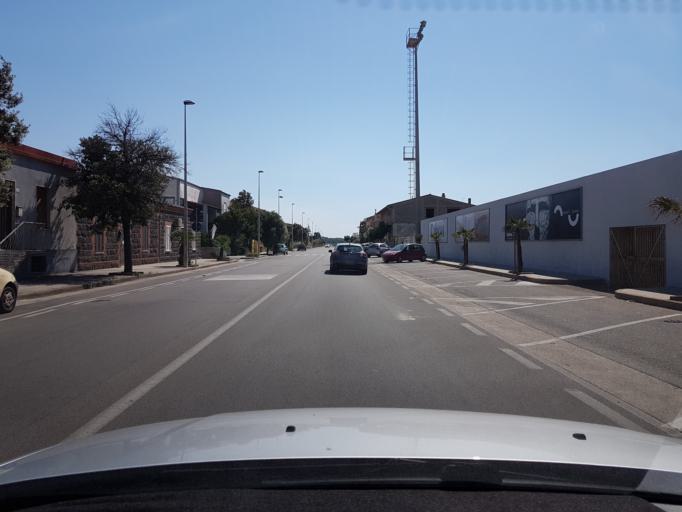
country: IT
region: Sardinia
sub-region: Provincia di Oristano
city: Cabras
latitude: 39.9232
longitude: 8.5246
